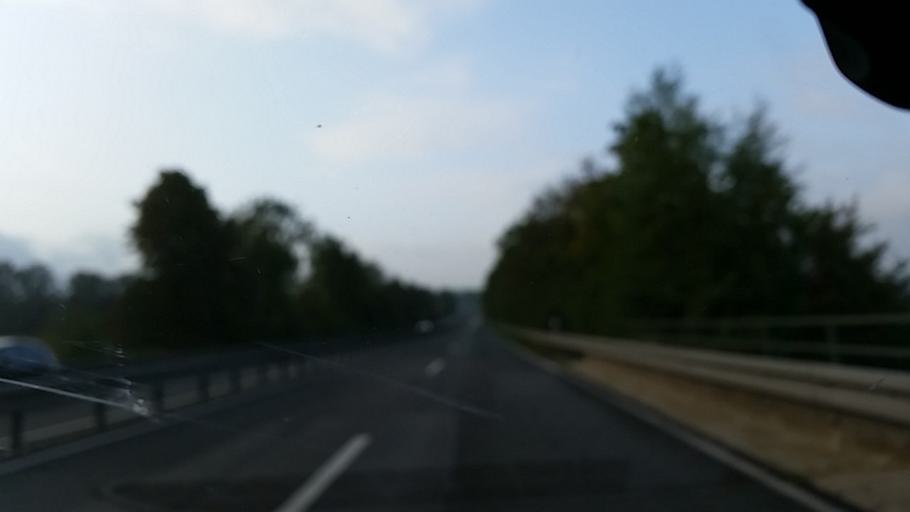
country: DE
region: Lower Saxony
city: Gittelde
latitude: 51.7932
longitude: 10.1966
